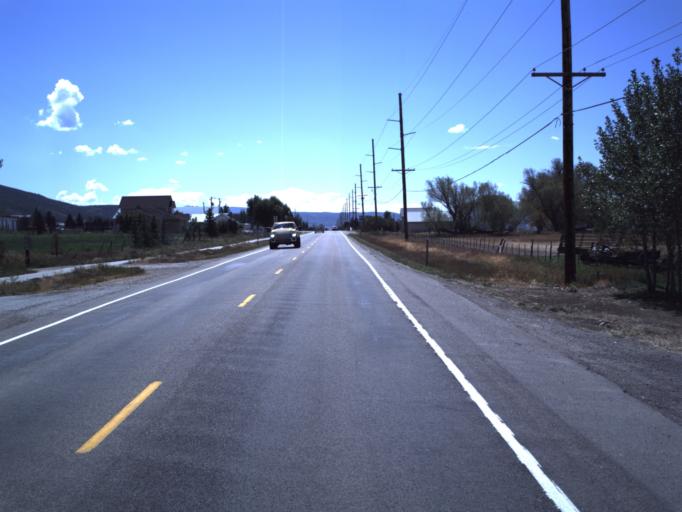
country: US
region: Utah
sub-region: Summit County
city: Oakley
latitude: 40.6938
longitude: -111.2810
